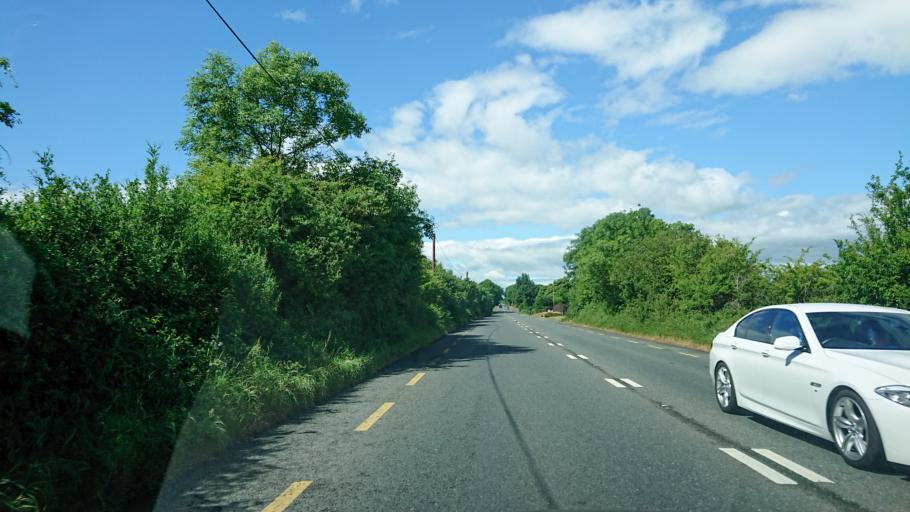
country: IE
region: Munster
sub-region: Waterford
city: Waterford
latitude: 52.2375
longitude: -7.1807
